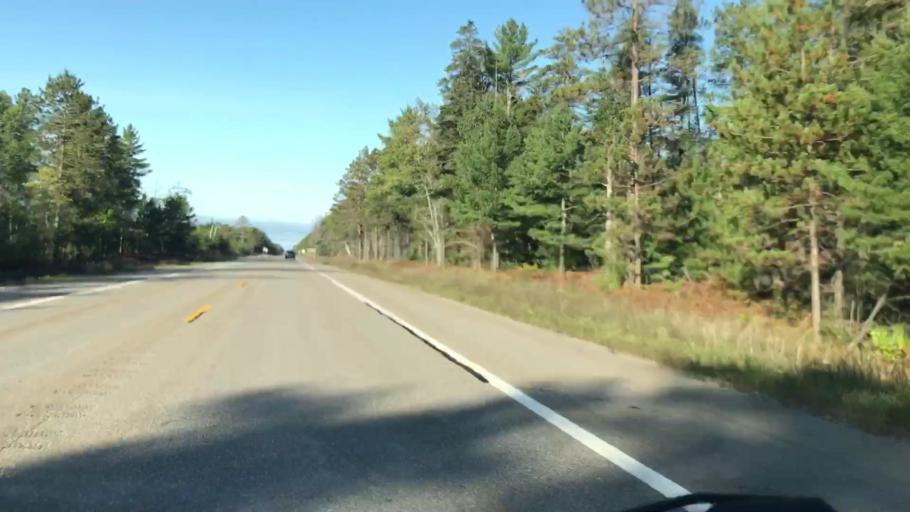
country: US
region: Michigan
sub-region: Chippewa County
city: Sault Ste. Marie
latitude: 46.3706
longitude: -84.7326
